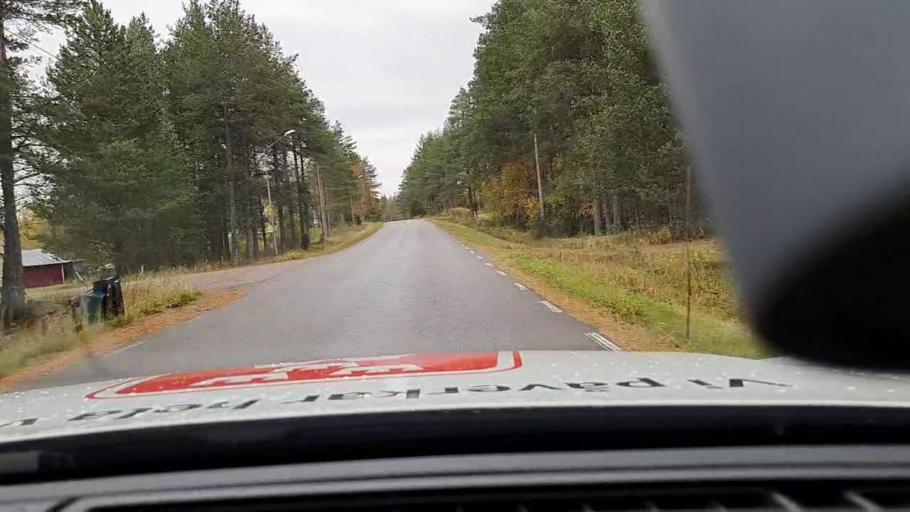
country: SE
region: Norrbotten
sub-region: Haparanda Kommun
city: Haparanda
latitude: 65.7834
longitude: 23.9197
